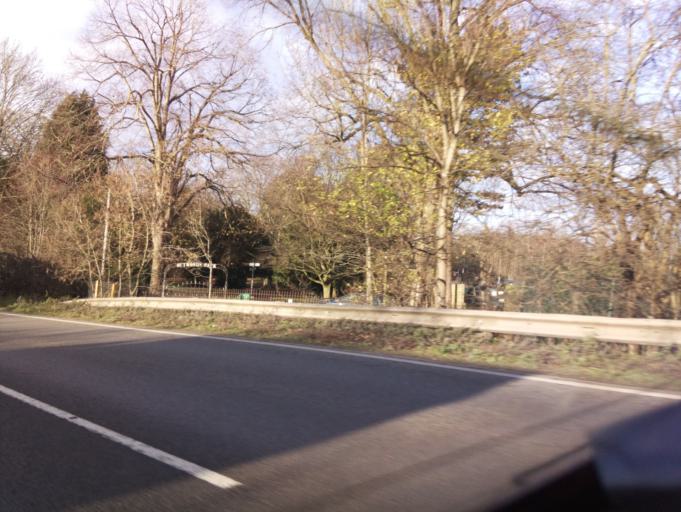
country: GB
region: England
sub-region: Staffordshire
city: Burton upon Trent
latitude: 52.8147
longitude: -1.6545
